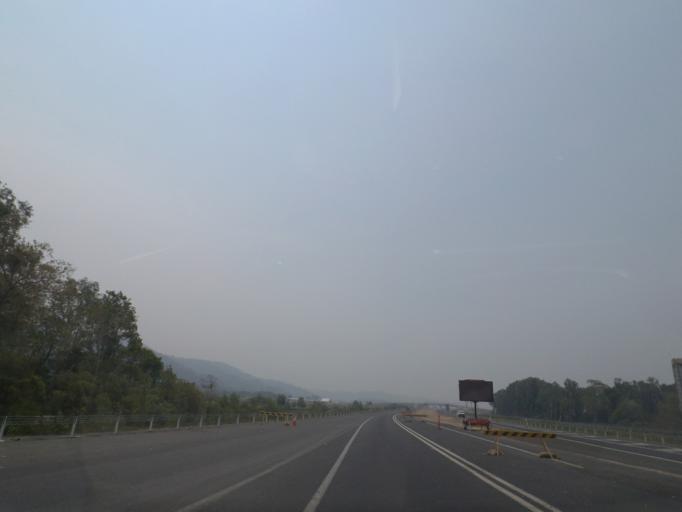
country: AU
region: New South Wales
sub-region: Ballina
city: Ballina
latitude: -28.9080
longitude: 153.4788
